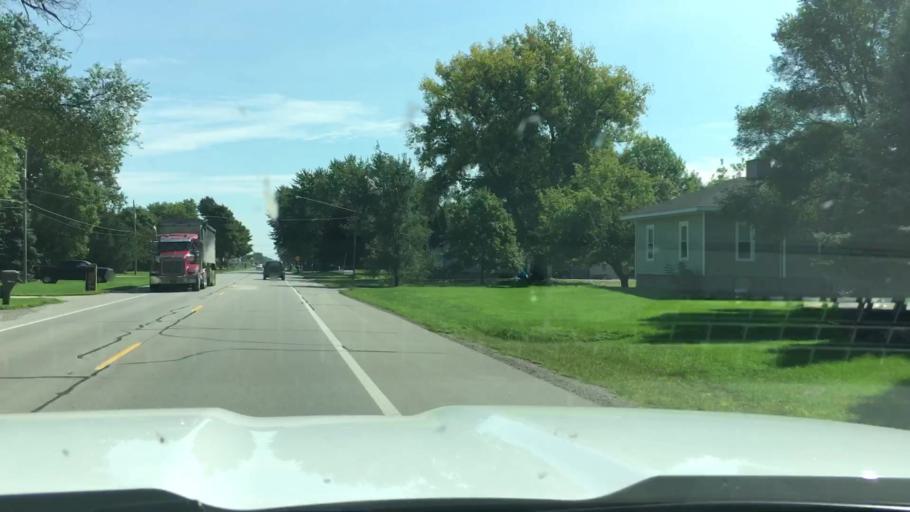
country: US
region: Michigan
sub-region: Bay County
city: Essexville
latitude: 43.5940
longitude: -83.8145
